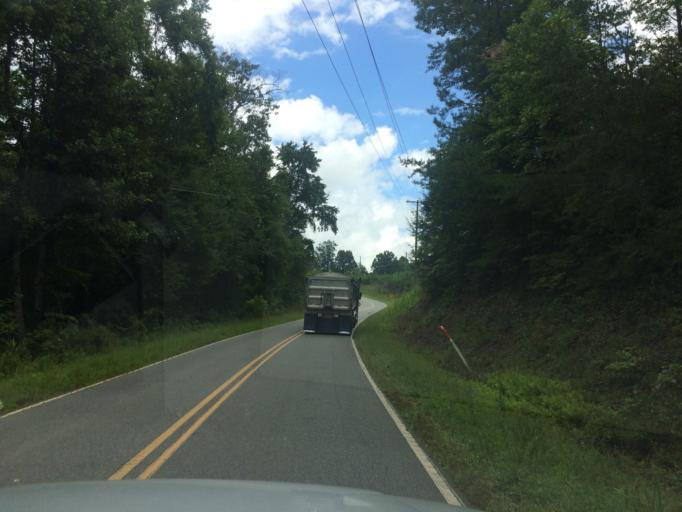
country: US
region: North Carolina
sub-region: Rutherford County
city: Lake Lure
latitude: 35.3916
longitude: -82.1917
